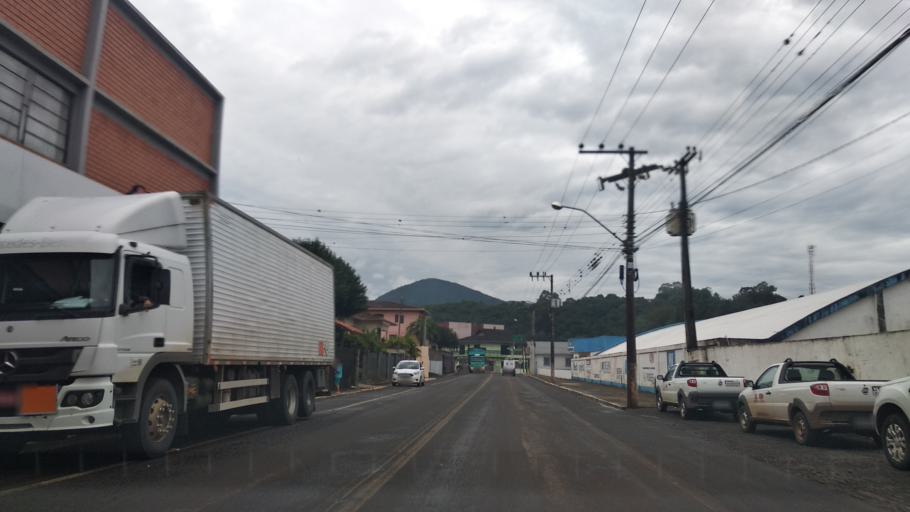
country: BR
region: Santa Catarina
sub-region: Videira
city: Videira
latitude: -27.1015
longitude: -51.2493
